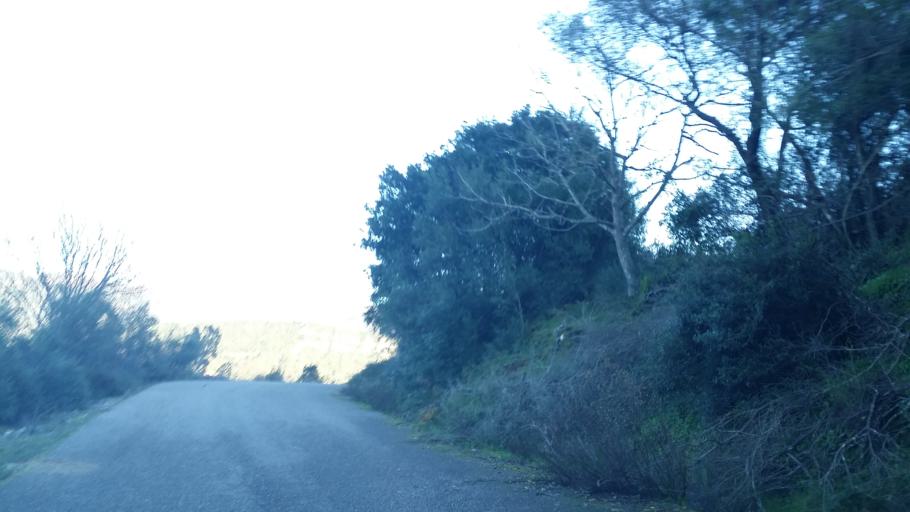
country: GR
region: West Greece
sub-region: Nomos Aitolias kai Akarnanias
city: Lepenou
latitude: 38.8193
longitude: 21.3320
